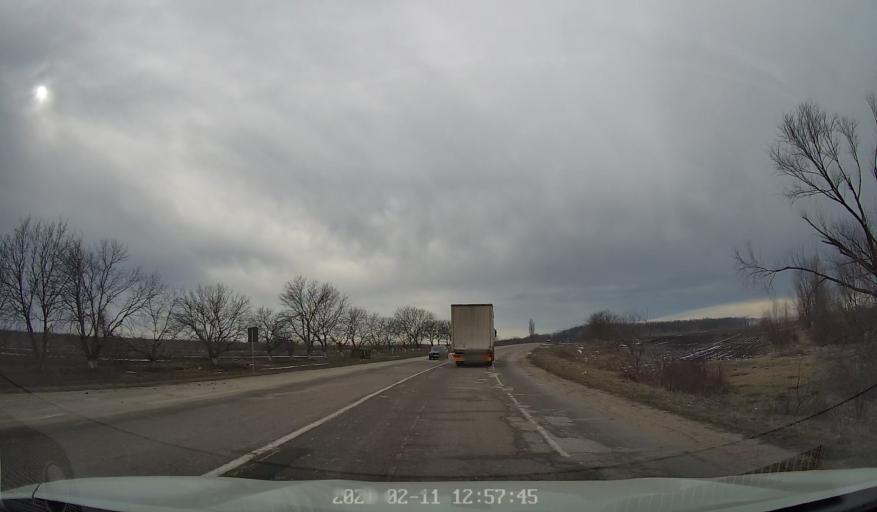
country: MD
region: Briceni
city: Briceni
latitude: 48.3383
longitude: 27.0641
